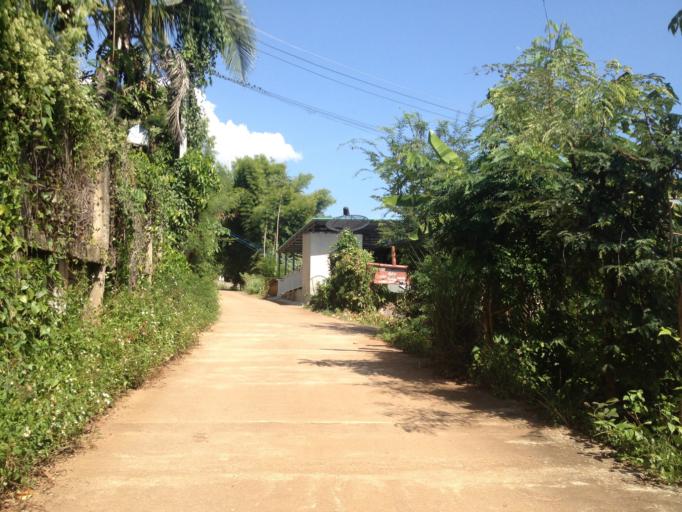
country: TH
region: Chiang Mai
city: Hang Dong
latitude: 18.7524
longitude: 98.8842
